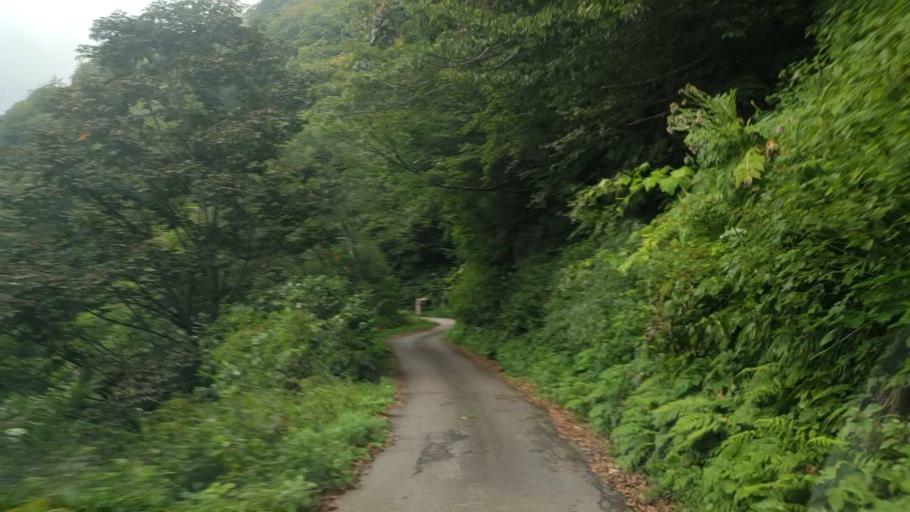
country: JP
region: Toyama
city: Yatsuomachi-higashikumisaka
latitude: 36.3953
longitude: 137.0777
